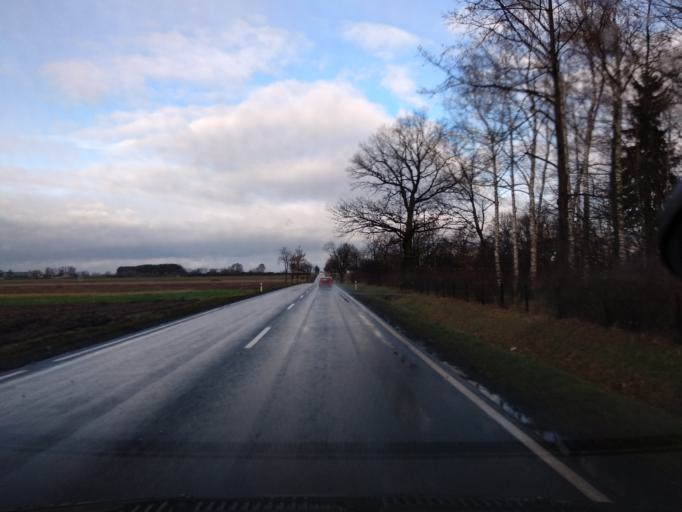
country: PL
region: Greater Poland Voivodeship
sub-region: Powiat koninski
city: Rychwal
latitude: 52.0459
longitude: 18.1624
